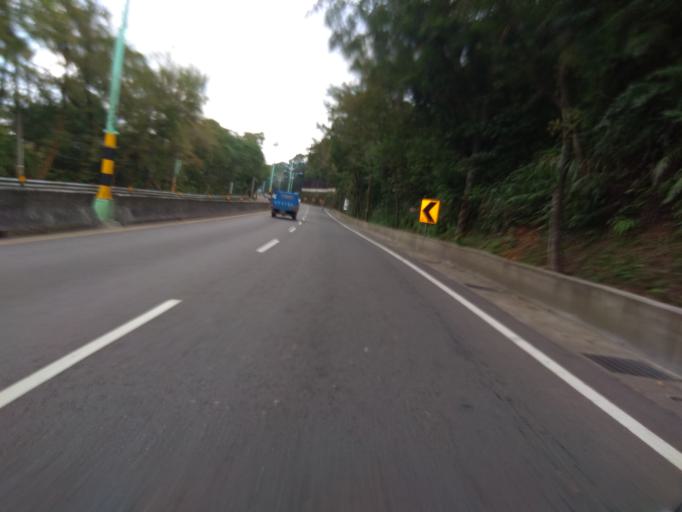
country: TW
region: Taiwan
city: Daxi
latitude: 24.8512
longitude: 121.2048
